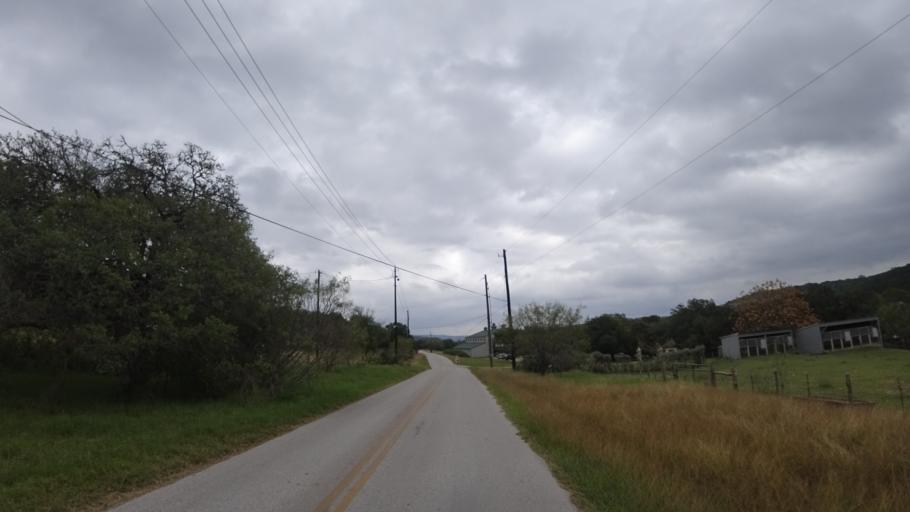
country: US
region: Texas
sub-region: Travis County
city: Bee Cave
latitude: 30.3370
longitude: -97.9080
